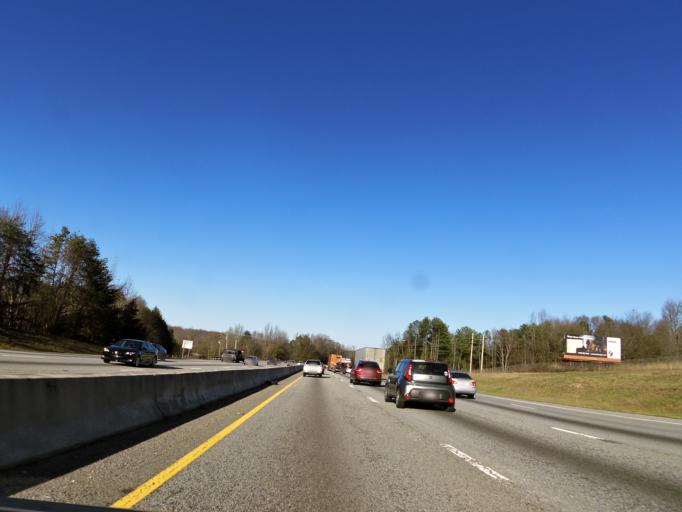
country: US
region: South Carolina
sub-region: Greenville County
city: Five Forks
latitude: 34.8481
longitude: -82.2797
